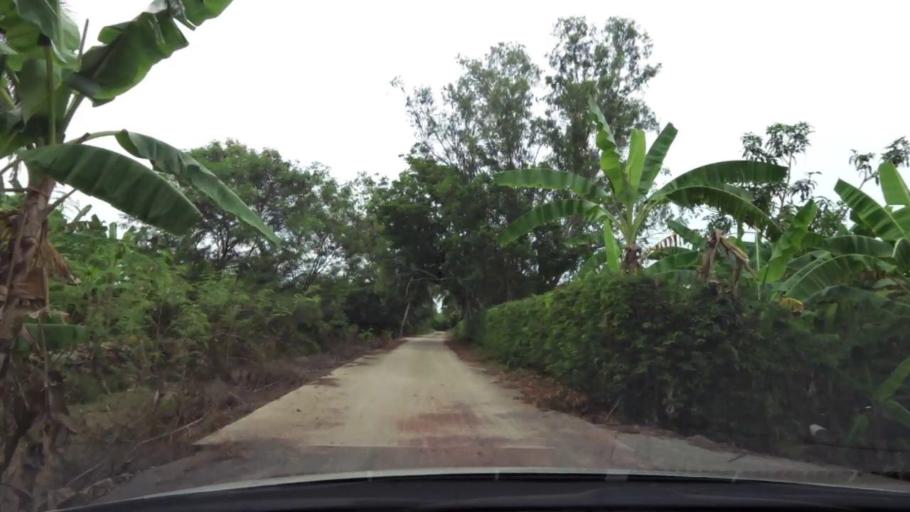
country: TH
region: Samut Sakhon
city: Ban Phaeo
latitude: 13.5923
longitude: 100.0346
